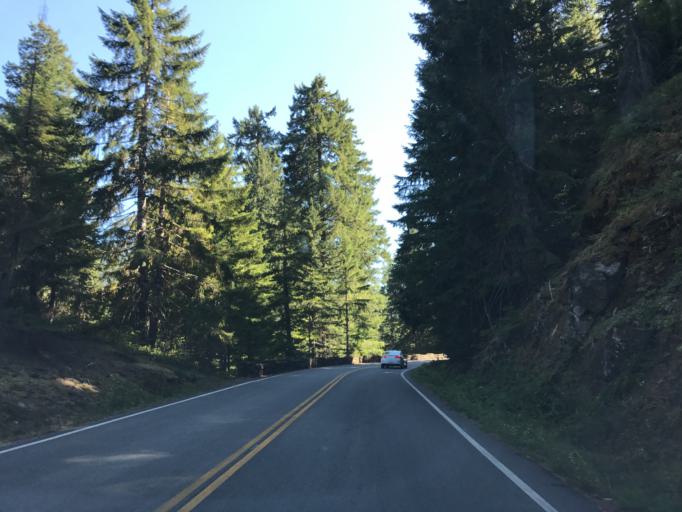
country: US
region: Washington
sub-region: Pierce County
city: Buckley
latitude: 46.7522
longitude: -121.5651
